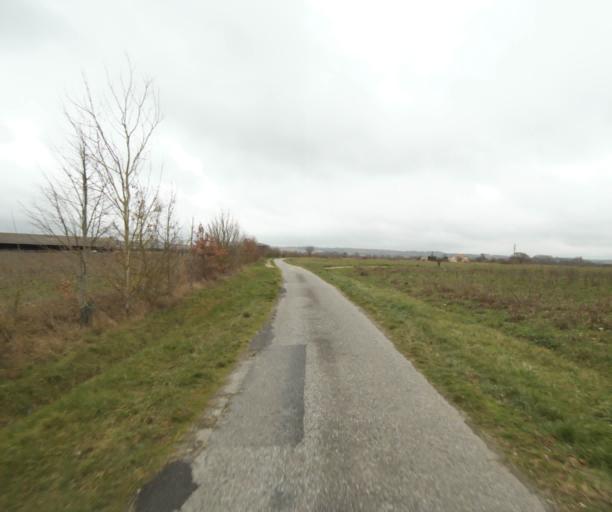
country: FR
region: Midi-Pyrenees
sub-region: Departement de l'Ariege
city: Mazeres
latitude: 43.2476
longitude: 1.6570
